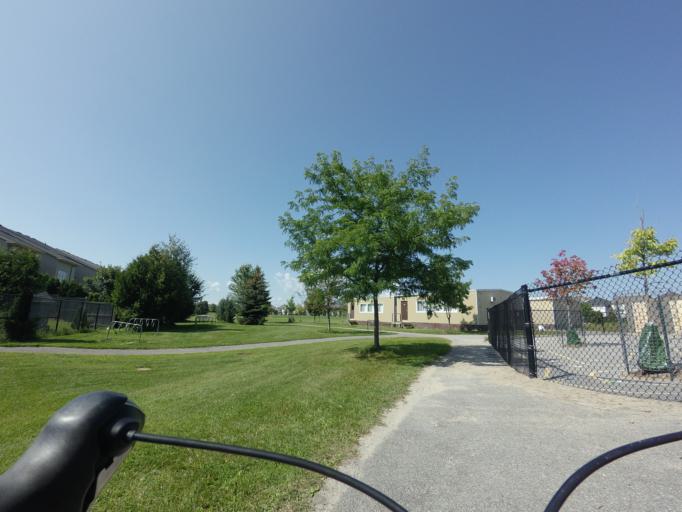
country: CA
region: Ontario
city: Bells Corners
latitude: 45.2832
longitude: -75.8469
